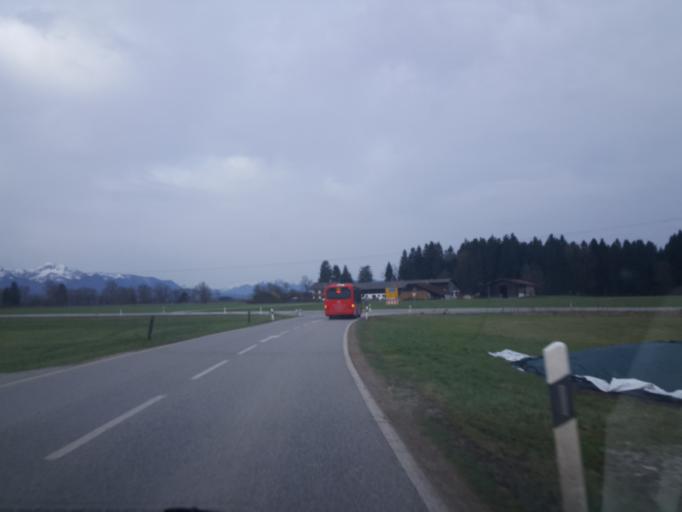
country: DE
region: Bavaria
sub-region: Upper Bavaria
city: Bichl
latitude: 47.7383
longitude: 11.4161
